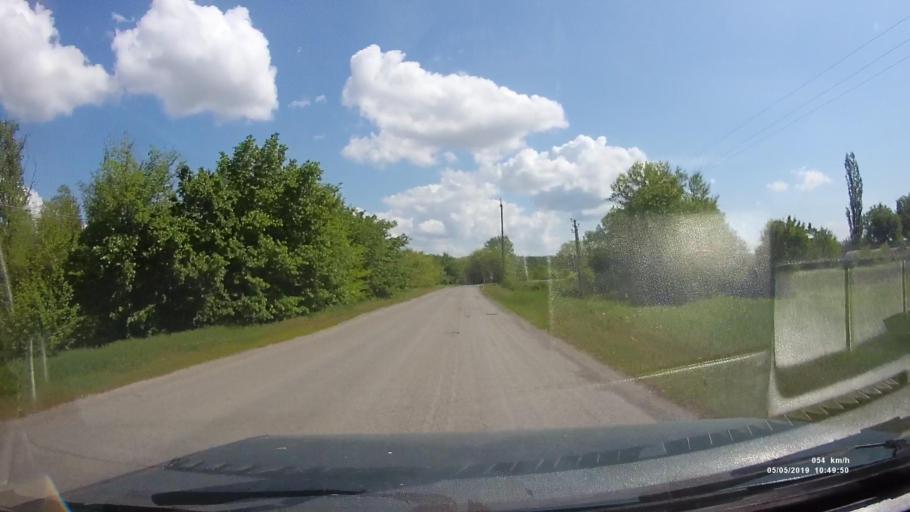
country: RU
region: Rostov
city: Ust'-Donetskiy
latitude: 47.6465
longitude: 40.8191
